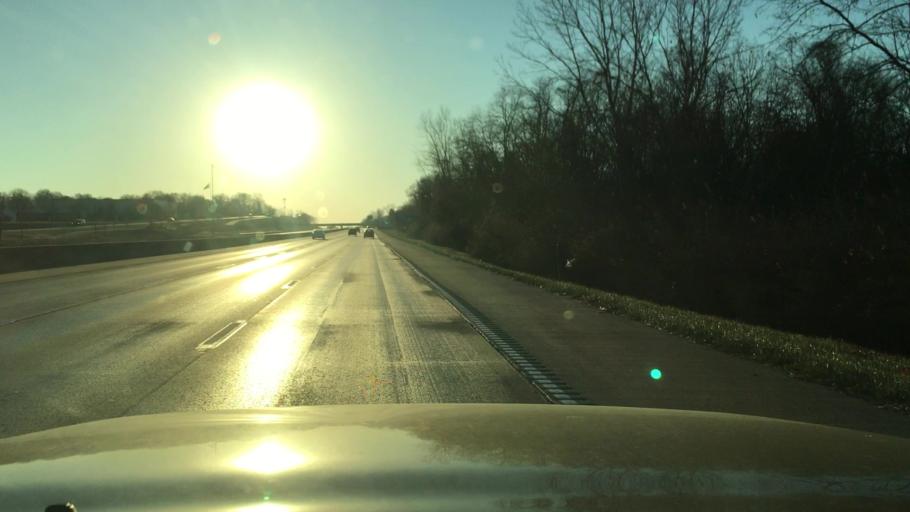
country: US
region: Missouri
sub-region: Saint Charles County
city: Saint Charles
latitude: 38.8128
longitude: -90.4902
